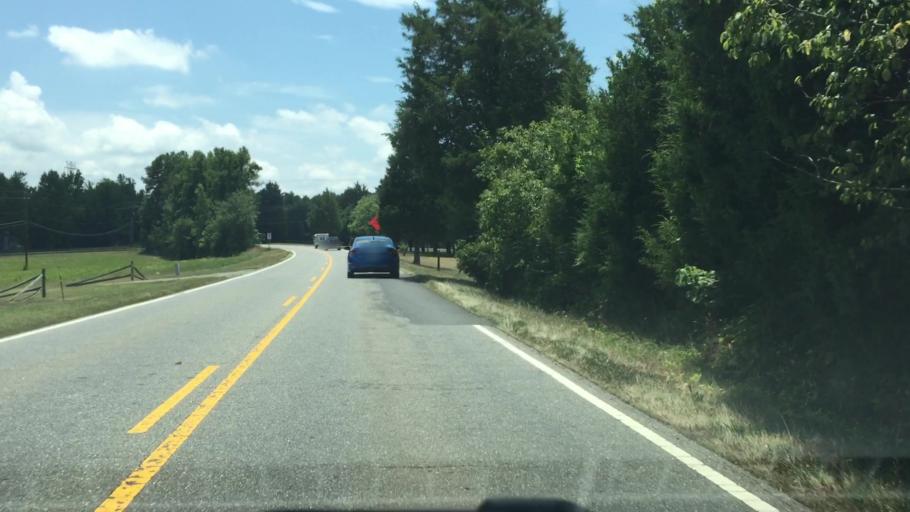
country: US
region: North Carolina
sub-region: Gaston County
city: Davidson
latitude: 35.5212
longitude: -80.7704
